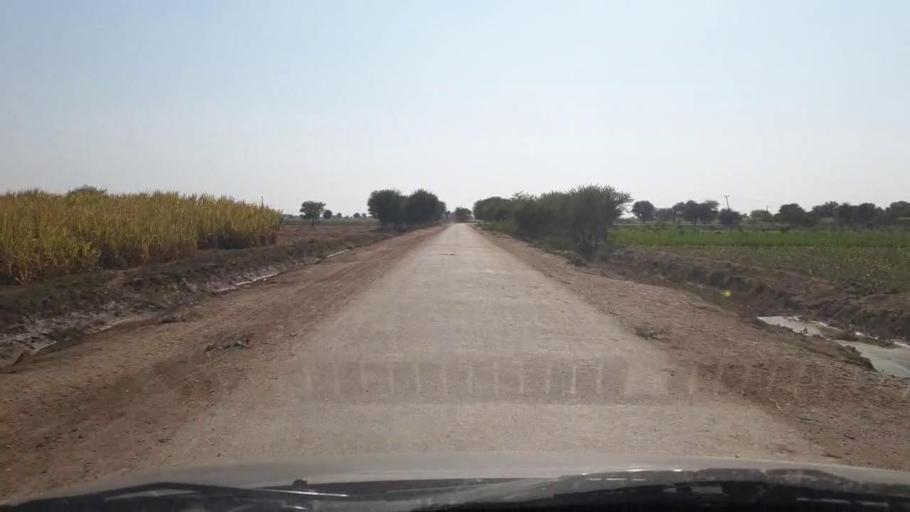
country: PK
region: Sindh
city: Samaro
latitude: 25.2134
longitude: 69.2713
